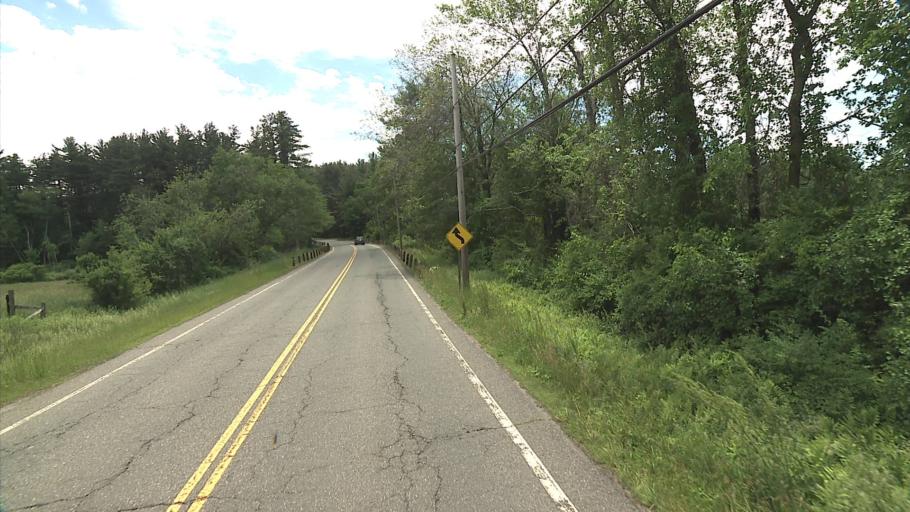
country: US
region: Connecticut
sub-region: Litchfield County
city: Litchfield
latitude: 41.7160
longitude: -73.1866
